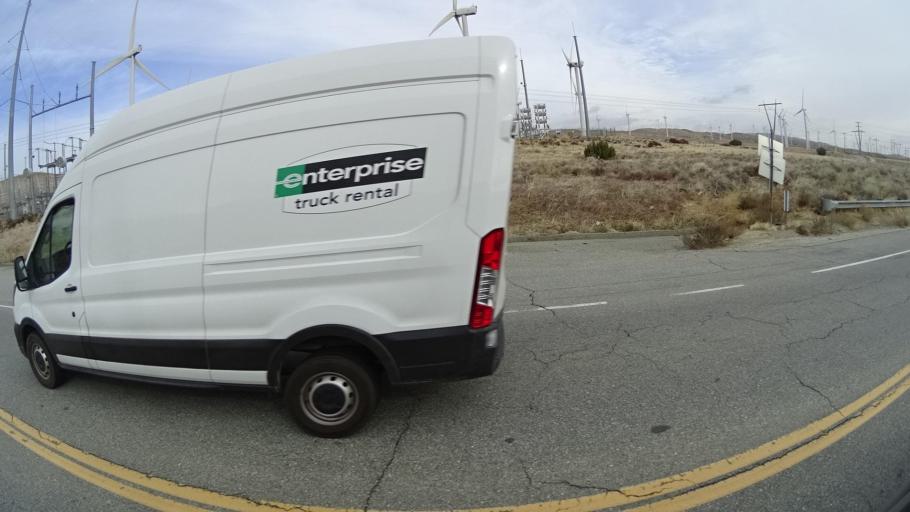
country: US
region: California
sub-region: Kern County
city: Tehachapi
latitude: 35.0525
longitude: -118.3599
